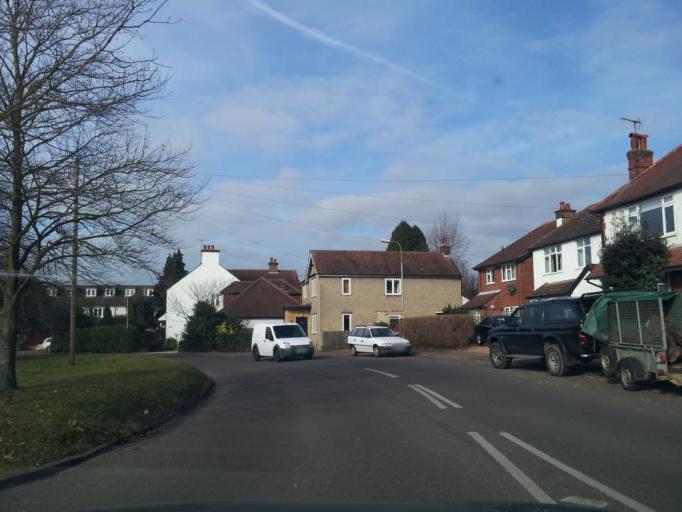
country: GB
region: England
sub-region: Hertfordshire
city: St Albans
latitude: 51.7460
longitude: -0.3043
